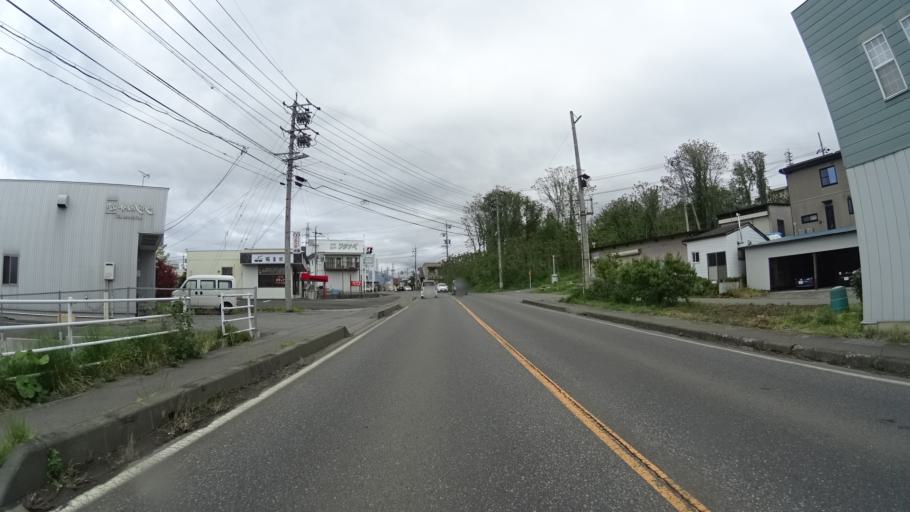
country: JP
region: Nagano
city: Nakano
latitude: 36.7342
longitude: 138.3232
